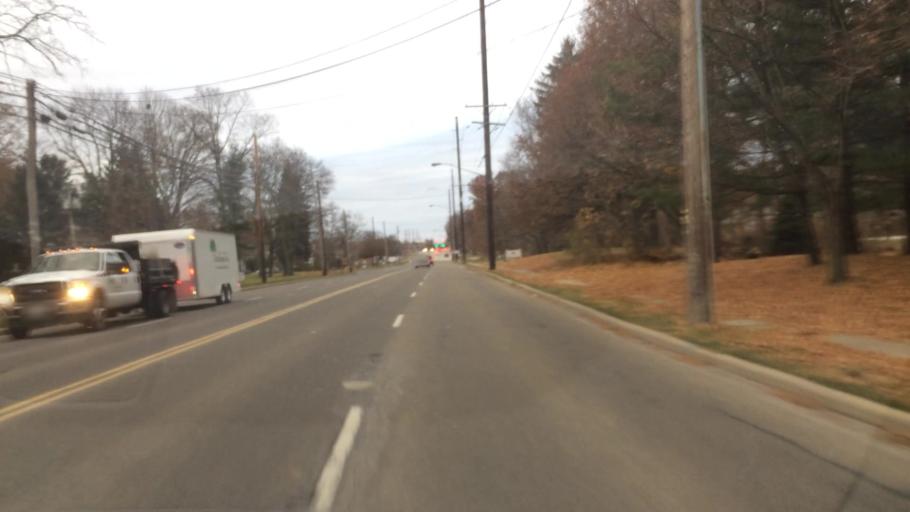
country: US
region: Ohio
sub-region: Summit County
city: Stow
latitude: 41.1741
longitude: -81.4404
